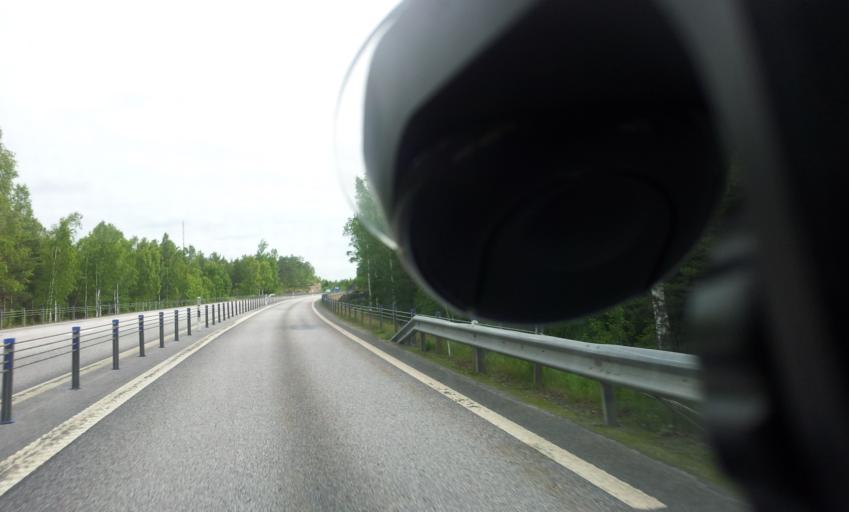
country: SE
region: OEstergoetland
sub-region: Valdemarsviks Kommun
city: Valdemarsvik
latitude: 58.1461
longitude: 16.5363
